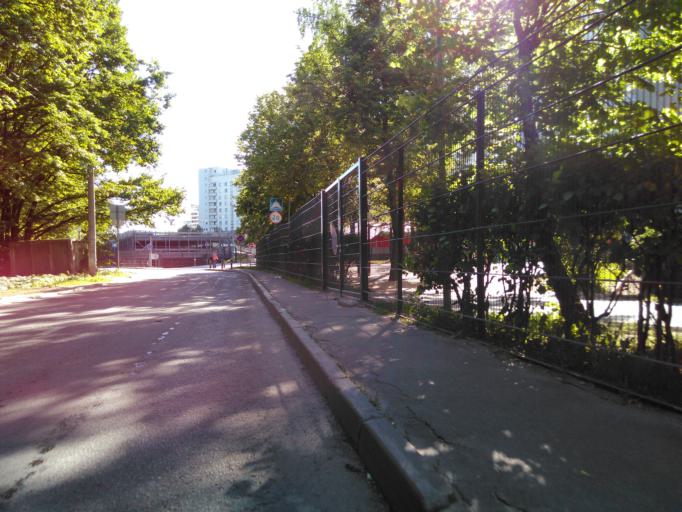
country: RU
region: Moscow
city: Troparevo
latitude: 55.6640
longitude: 37.4959
